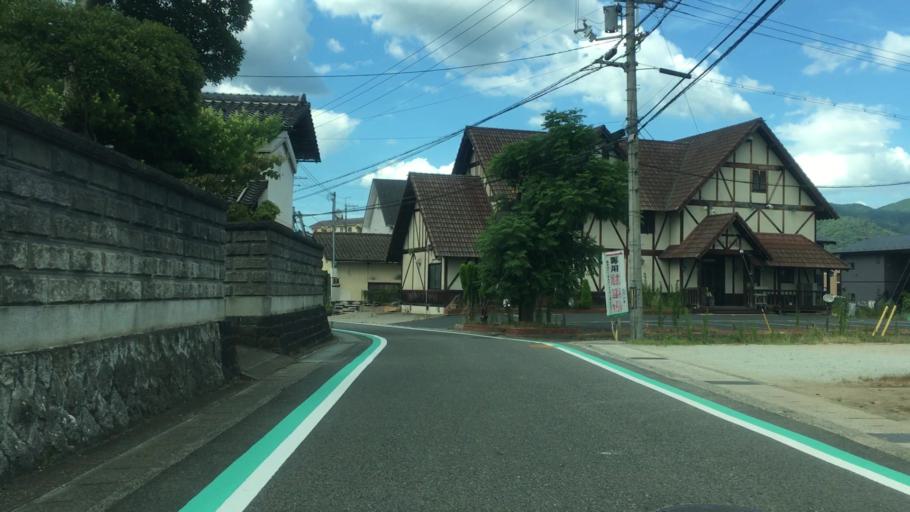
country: JP
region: Hyogo
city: Toyooka
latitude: 35.5554
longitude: 134.8056
